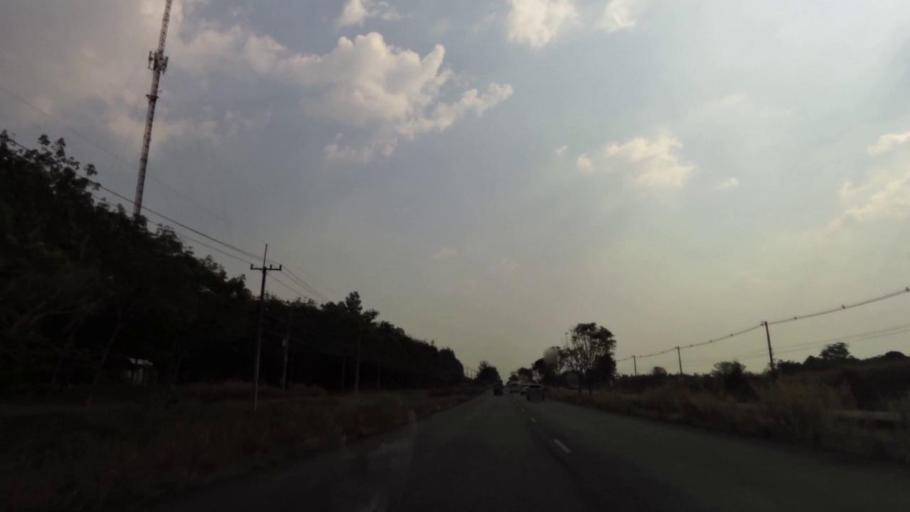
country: TH
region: Rayong
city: Wang Chan
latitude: 12.9860
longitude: 101.4892
